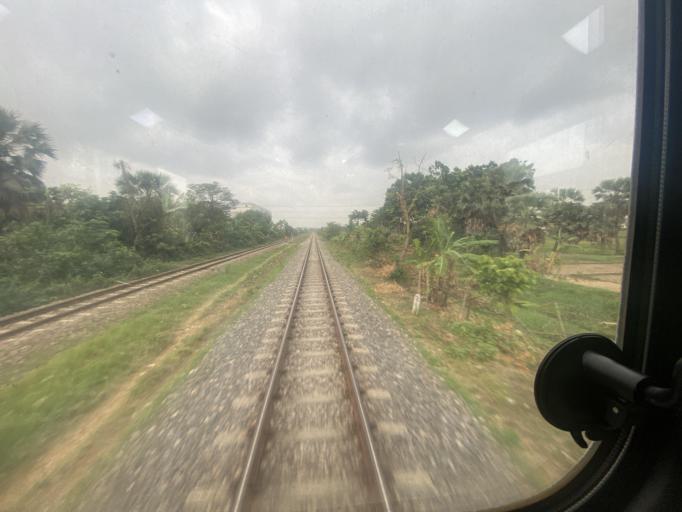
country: BD
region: Dhaka
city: Tungi
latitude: 23.9123
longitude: 90.4193
